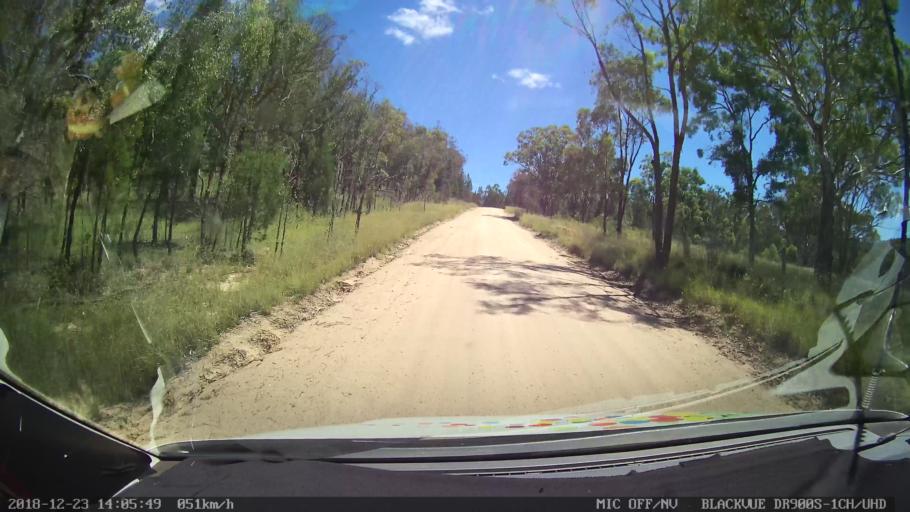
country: AU
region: New South Wales
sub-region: Tamworth Municipality
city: Manilla
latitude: -30.6264
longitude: 151.0781
